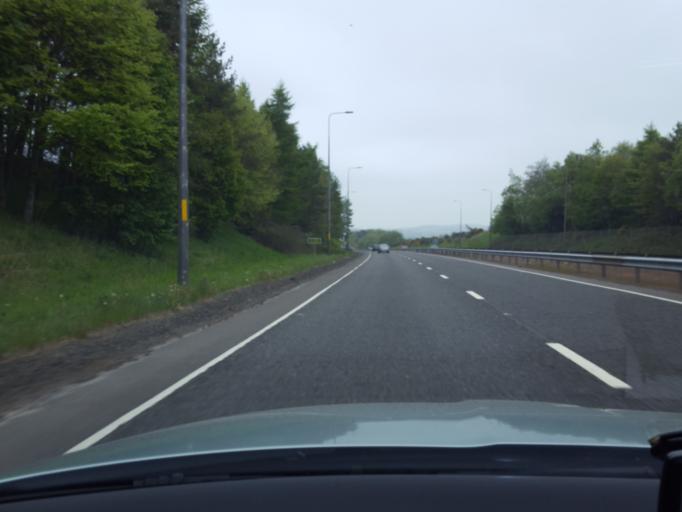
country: GB
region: Scotland
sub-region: Angus
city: Forfar
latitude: 56.5777
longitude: -2.9137
